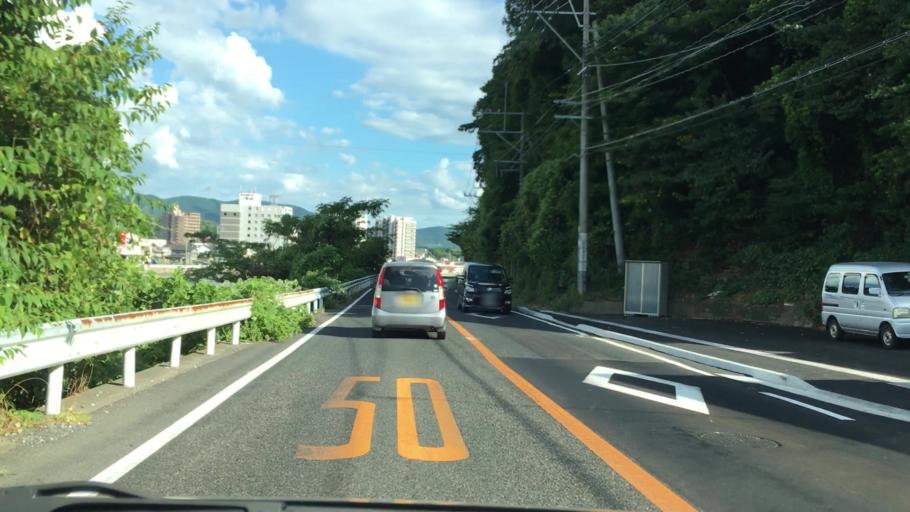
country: JP
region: Nagasaki
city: Sasebo
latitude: 33.1365
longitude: 129.7944
